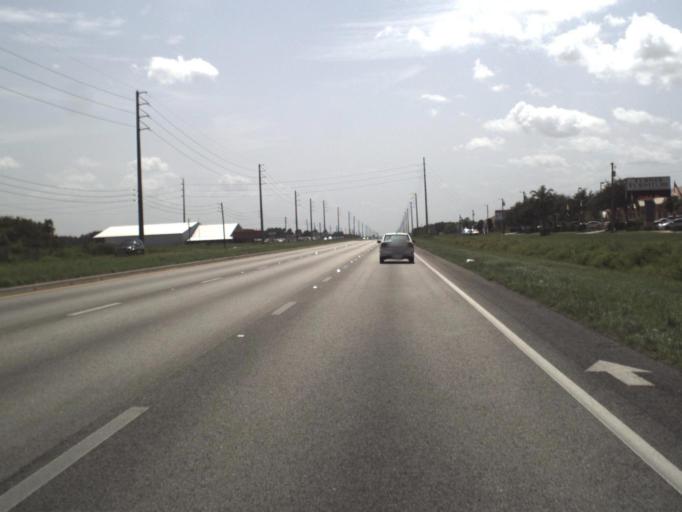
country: US
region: Florida
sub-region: Highlands County
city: Avon Park
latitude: 27.5555
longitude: -81.5101
